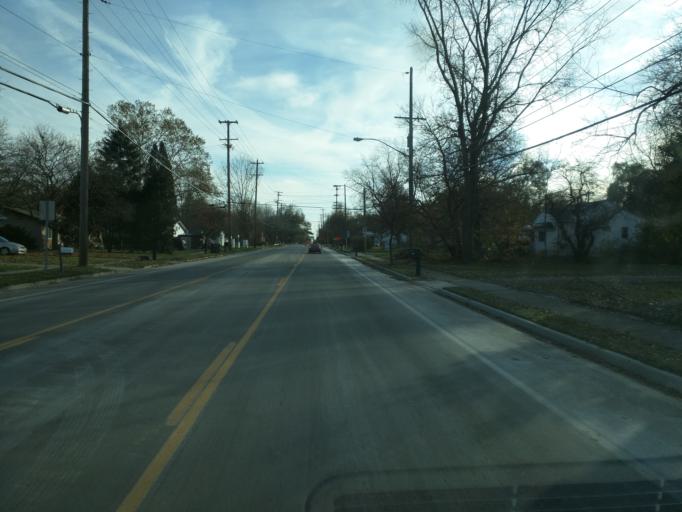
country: US
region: Michigan
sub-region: Eaton County
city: Waverly
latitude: 42.6831
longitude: -84.5943
